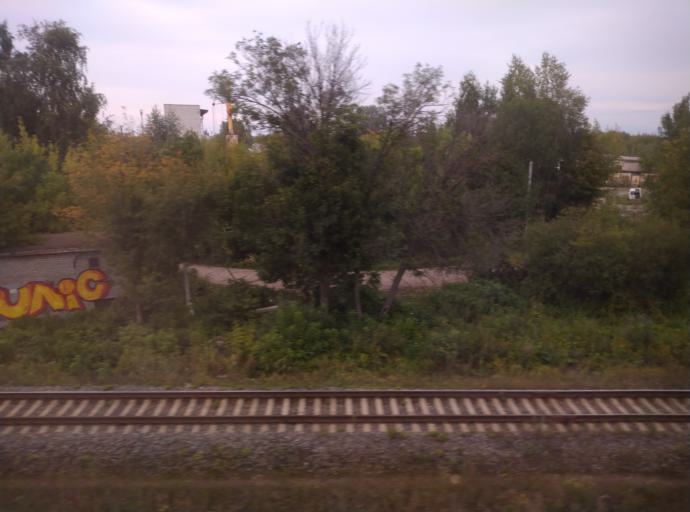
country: RU
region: Jaroslavl
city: Yaroslavl
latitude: 57.5997
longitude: 39.8907
